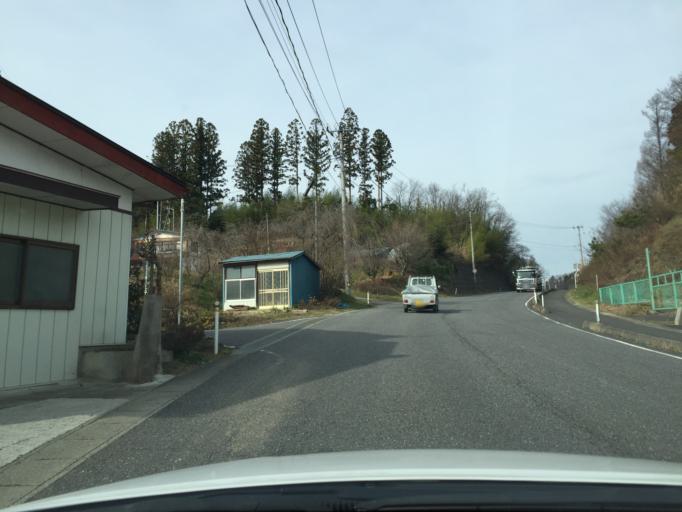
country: JP
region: Fukushima
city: Funehikimachi-funehiki
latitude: 37.4030
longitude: 140.5930
